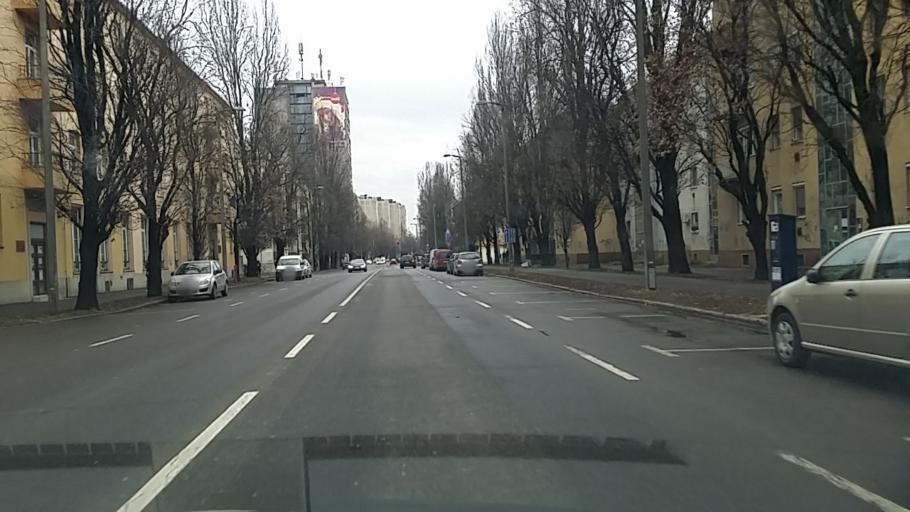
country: HU
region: Hajdu-Bihar
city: Debrecen
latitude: 47.5399
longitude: 21.6219
